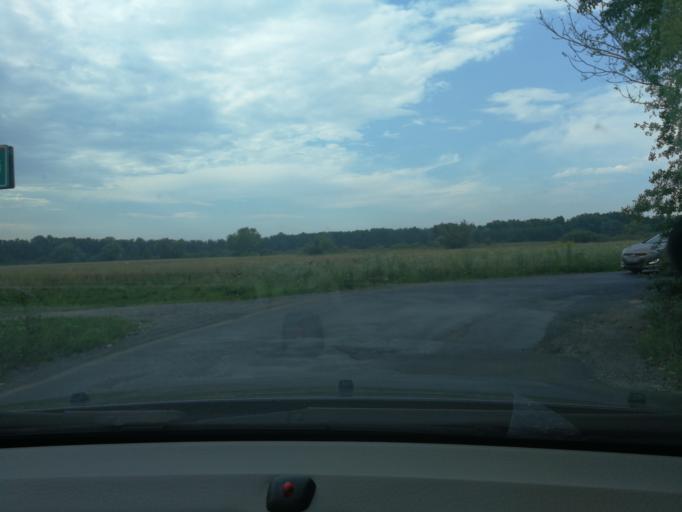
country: PL
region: Masovian Voivodeship
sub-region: Powiat warszawski zachodni
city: Bieniewice
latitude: 52.1128
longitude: 20.5533
